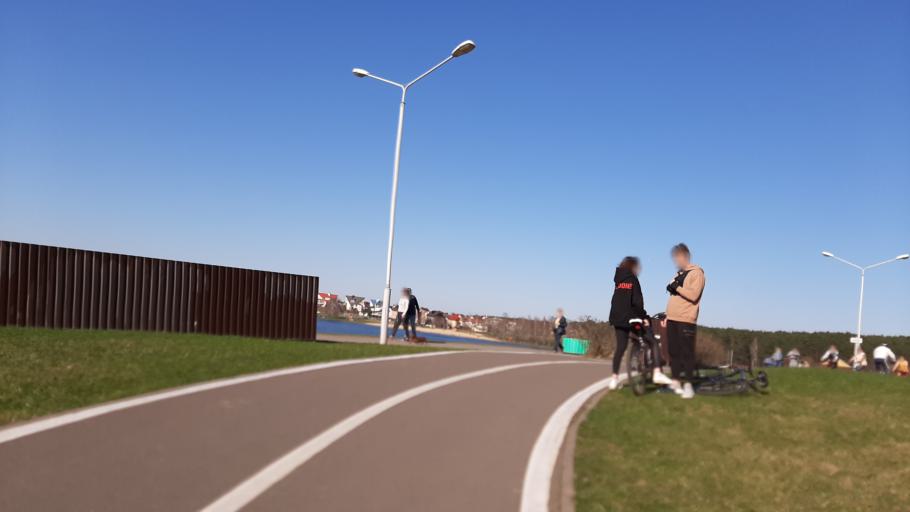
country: BY
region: Minsk
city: Bal'shavik
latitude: 53.9595
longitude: 27.5885
